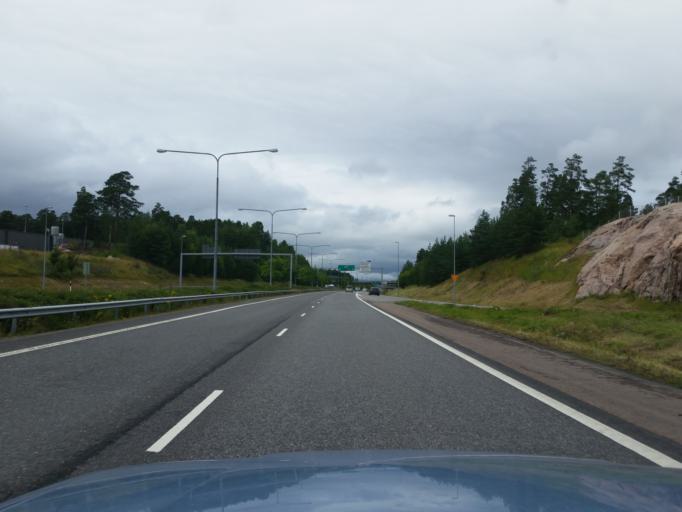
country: FI
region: Varsinais-Suomi
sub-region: Turku
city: Kaarina
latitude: 60.4302
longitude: 22.3259
